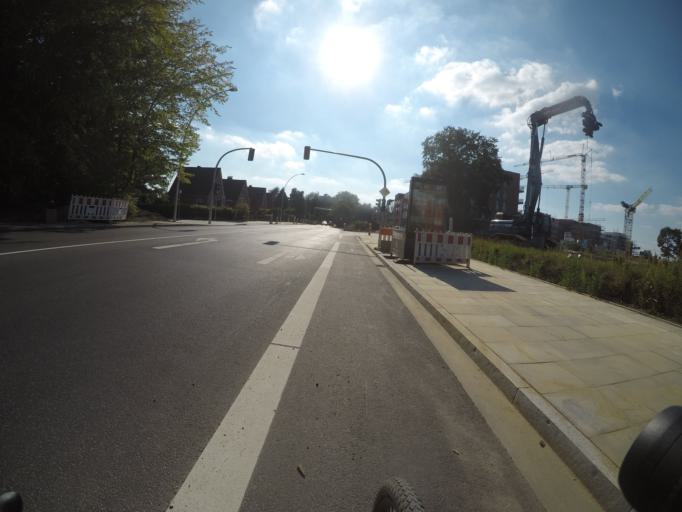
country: DE
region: Schleswig-Holstein
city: Glinde
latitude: 53.5125
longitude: 10.2017
